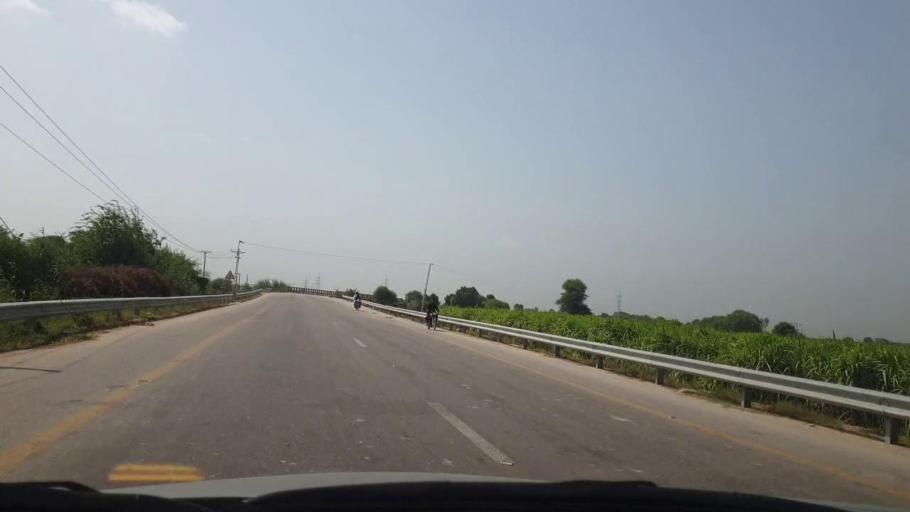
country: PK
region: Sindh
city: Matli
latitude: 25.0526
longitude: 68.6356
